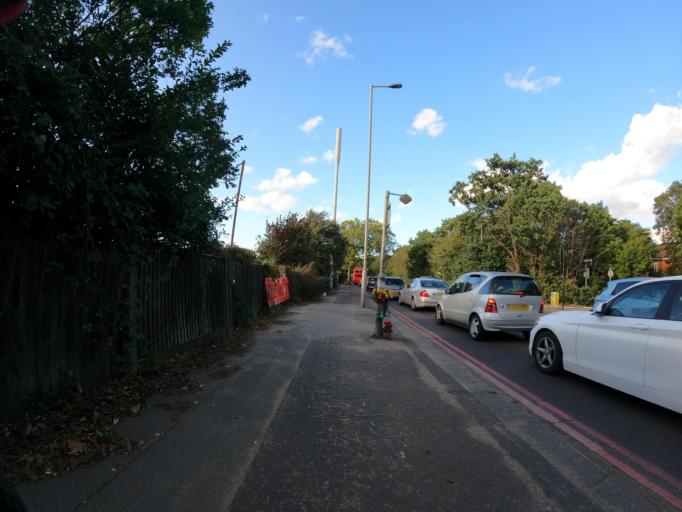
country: GB
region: England
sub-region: Greater London
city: Ealing Broadway
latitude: 51.5200
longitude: -0.2916
